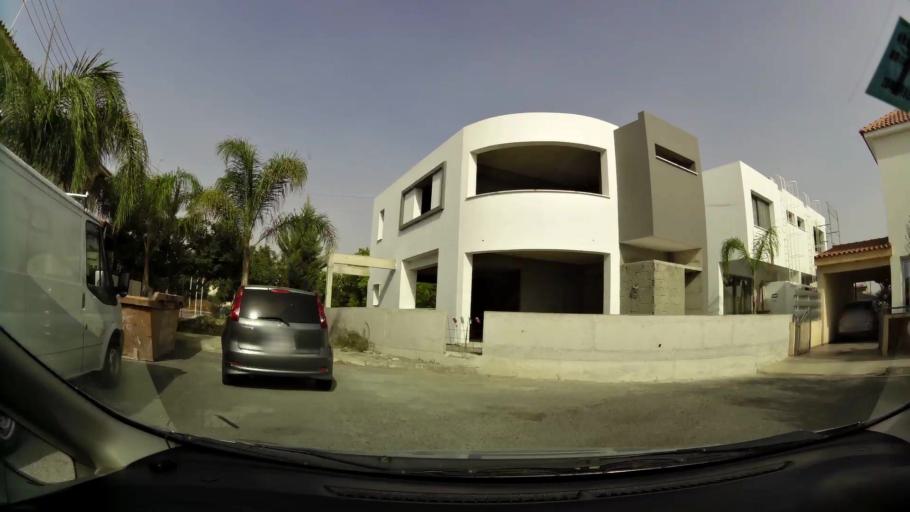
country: CY
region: Lefkosia
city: Geri
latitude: 35.0729
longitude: 33.3931
